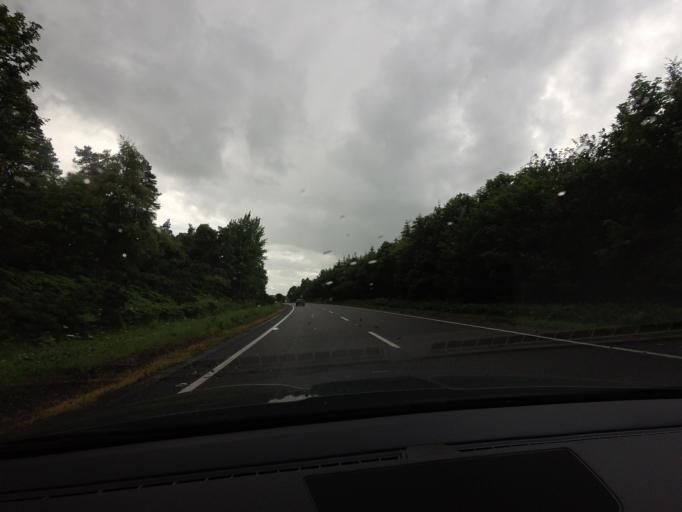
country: GB
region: Scotland
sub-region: Highland
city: Fortrose
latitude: 57.5268
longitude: -4.0579
